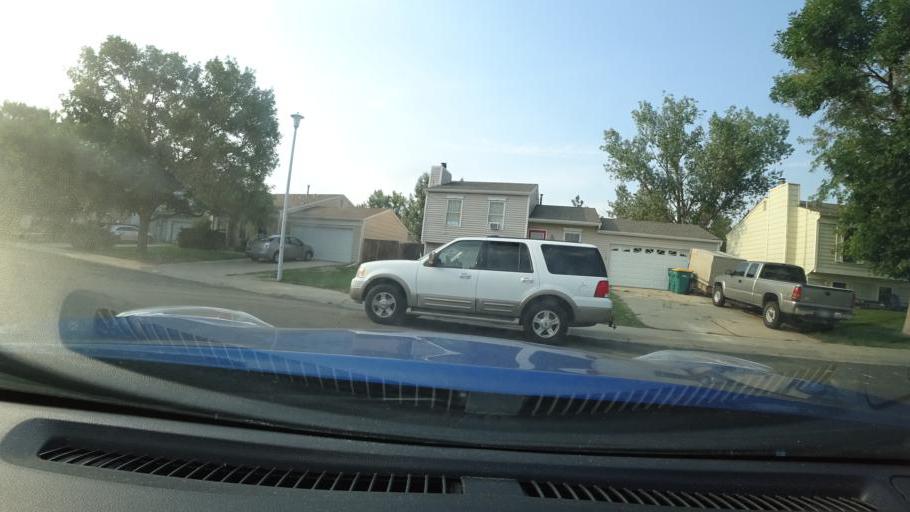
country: US
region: Colorado
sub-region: Adams County
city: Aurora
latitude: 39.7478
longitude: -104.7650
